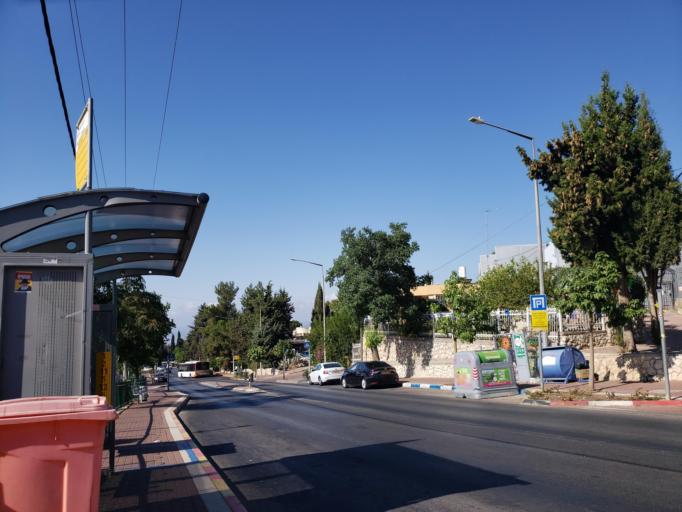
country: IL
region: Northern District
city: Safed
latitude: 32.9619
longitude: 35.4988
